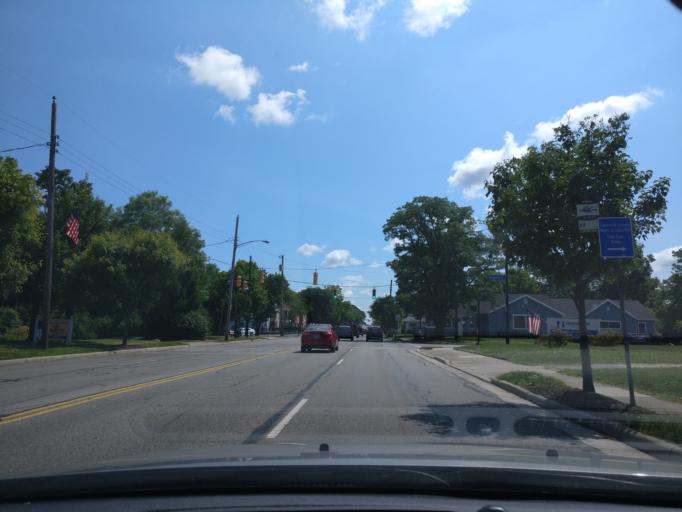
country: US
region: Ohio
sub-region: Montgomery County
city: Centerville
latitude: 39.6282
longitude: -84.1642
